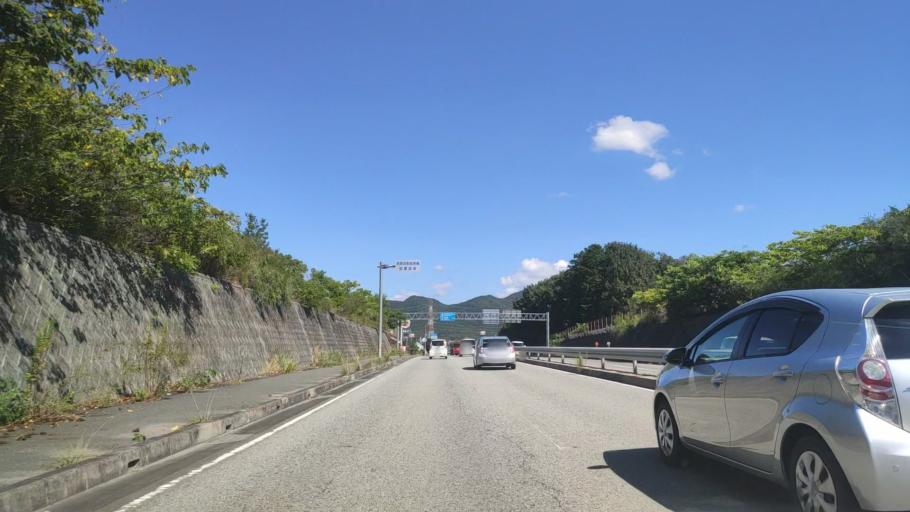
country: JP
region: Hyogo
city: Yashiro
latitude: 34.9472
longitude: 134.9693
